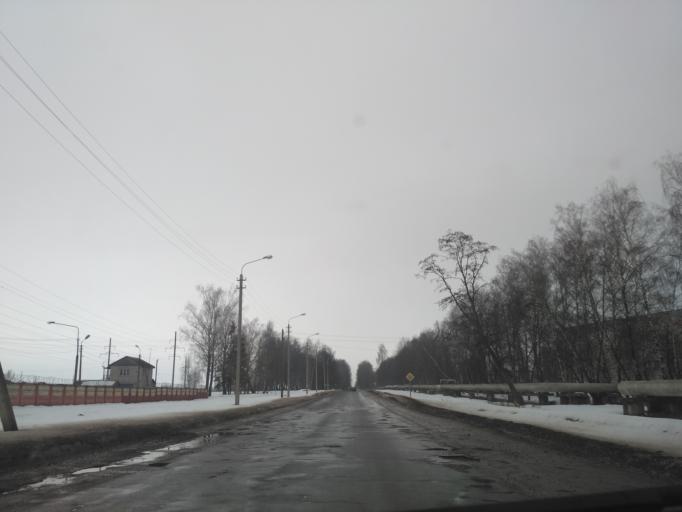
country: BY
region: Minsk
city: Horad Zhodzina
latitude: 54.0918
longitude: 28.3297
